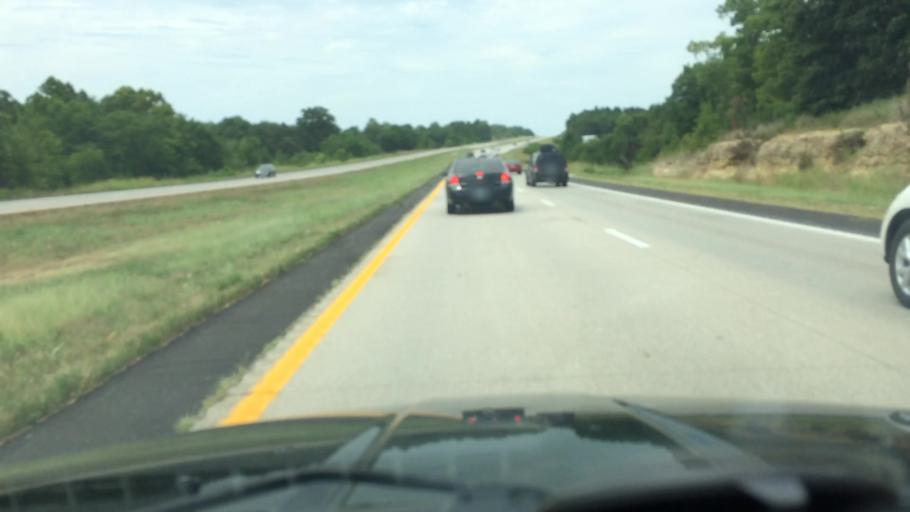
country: US
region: Missouri
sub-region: Greene County
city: Willard
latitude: 37.4322
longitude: -93.3553
